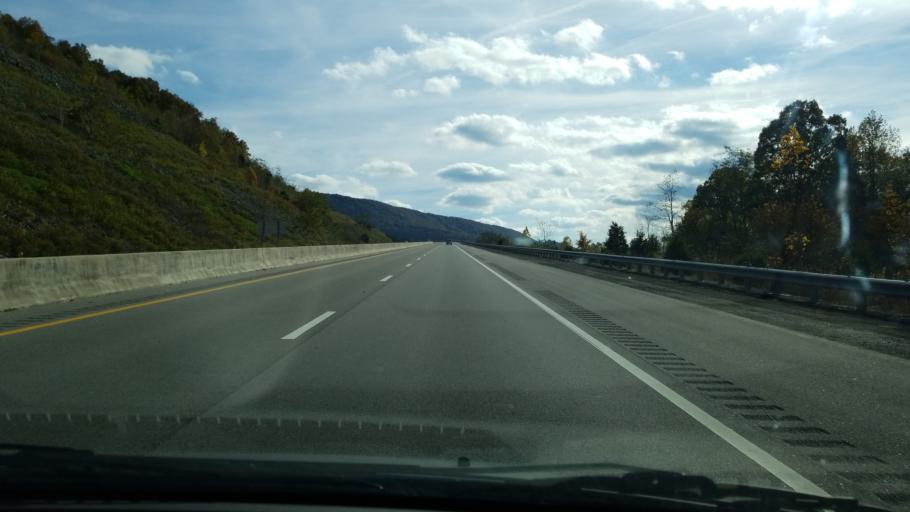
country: US
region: Tennessee
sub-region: Sequatchie County
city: Dunlap
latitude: 35.3765
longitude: -85.3317
